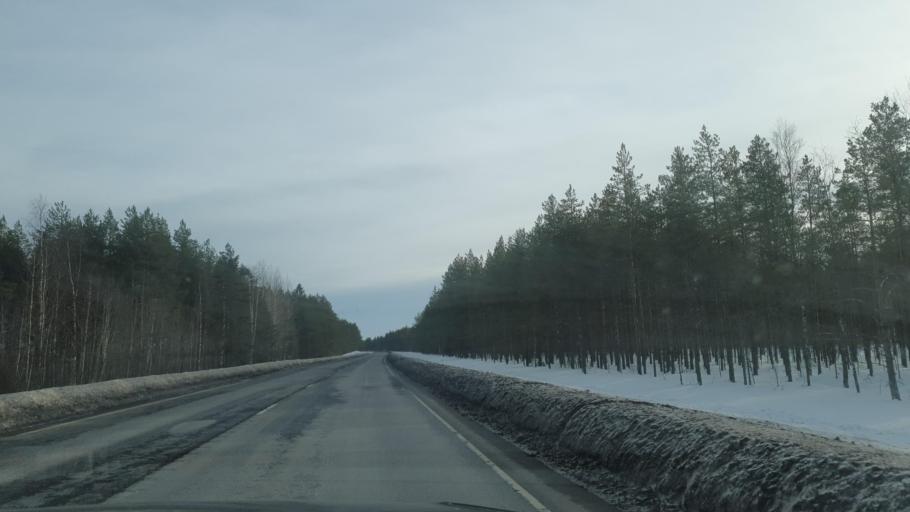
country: FI
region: Northern Ostrobothnia
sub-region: Oulunkaari
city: Utajaervi
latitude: 64.7316
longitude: 26.4799
